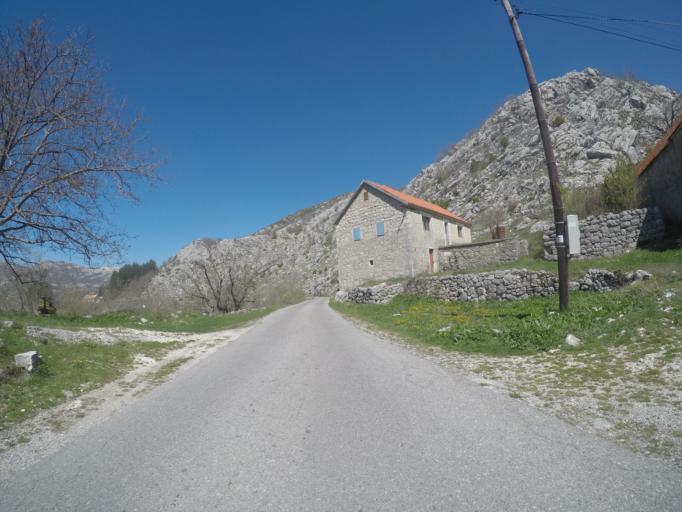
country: ME
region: Cetinje
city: Cetinje
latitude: 42.4583
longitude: 18.8730
